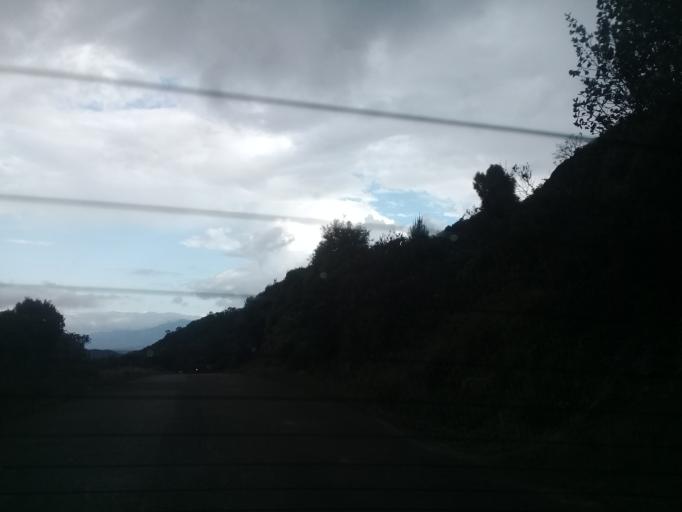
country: CO
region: Cundinamarca
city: Junin
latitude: 4.8544
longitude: -73.7486
